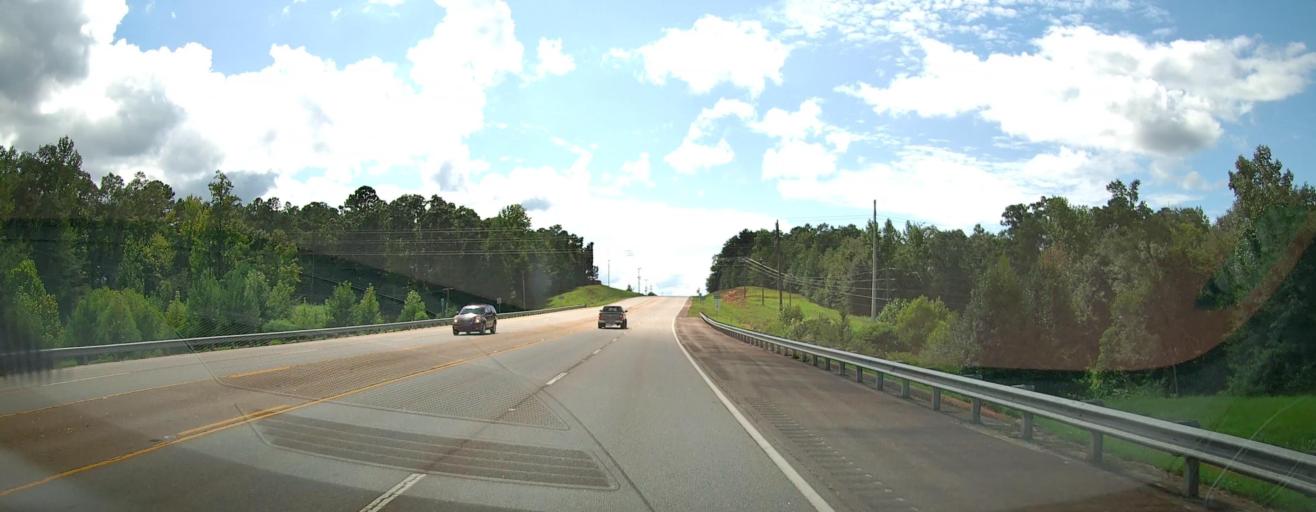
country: US
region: Georgia
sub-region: Upson County
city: Thomaston
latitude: 32.8881
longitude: -84.3051
